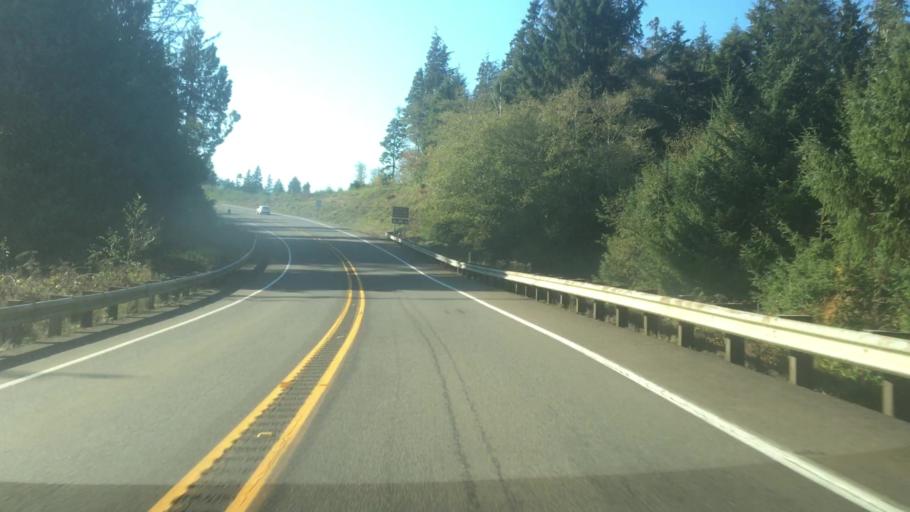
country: US
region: Washington
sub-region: Pacific County
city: South Bend
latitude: 46.6855
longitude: -123.8810
